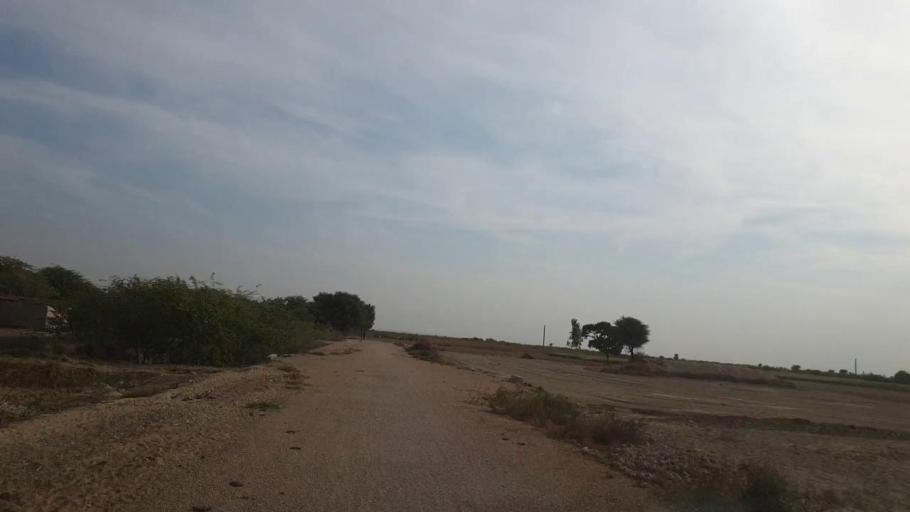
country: PK
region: Sindh
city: Nabisar
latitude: 24.9998
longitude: 69.5342
